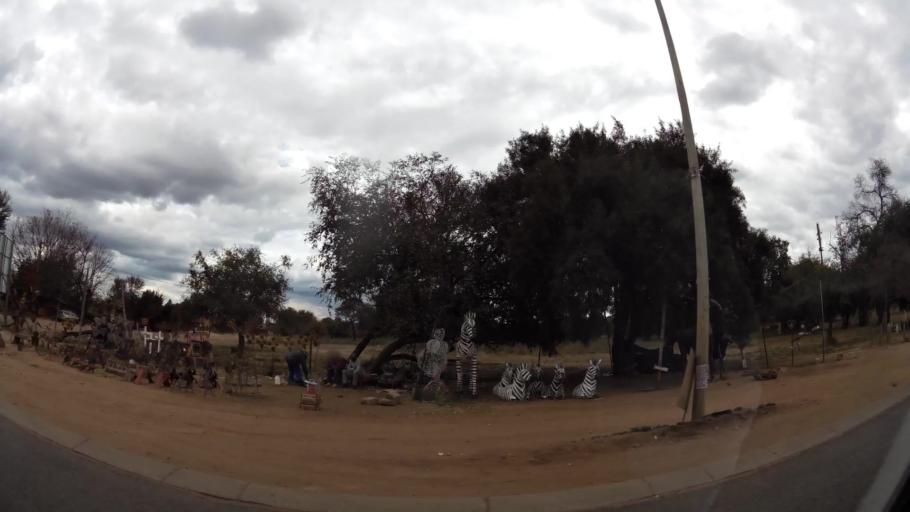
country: ZA
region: Limpopo
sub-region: Waterberg District Municipality
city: Modimolle
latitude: -24.7086
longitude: 28.4136
